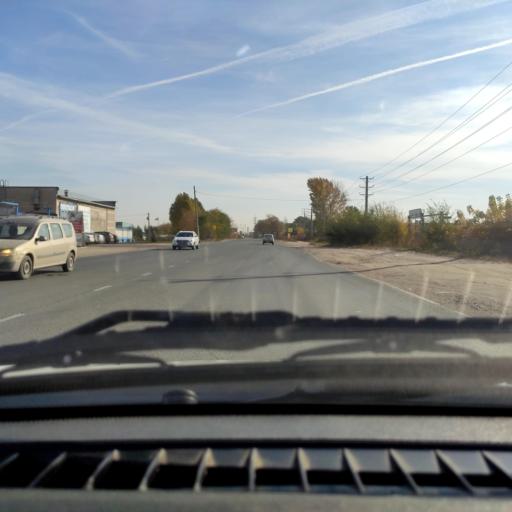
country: RU
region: Samara
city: Tol'yatti
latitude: 53.5304
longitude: 49.4647
